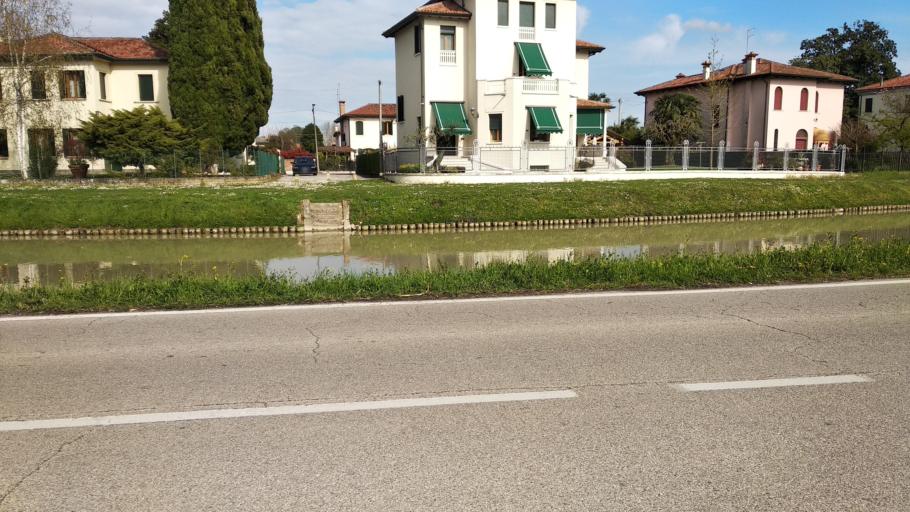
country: IT
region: Veneto
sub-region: Provincia di Venezia
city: Mira Taglio
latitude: 45.4365
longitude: 12.1370
